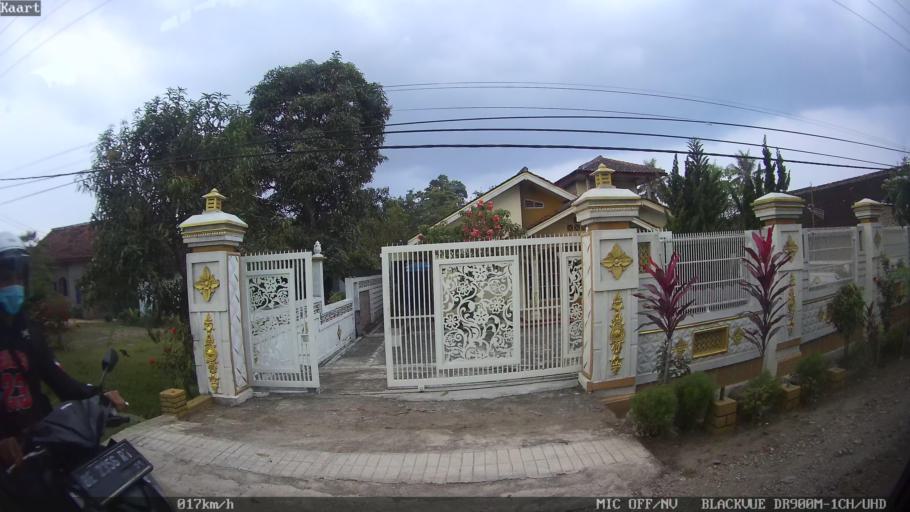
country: ID
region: Lampung
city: Gadingrejo
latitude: -5.3721
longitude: 105.0772
